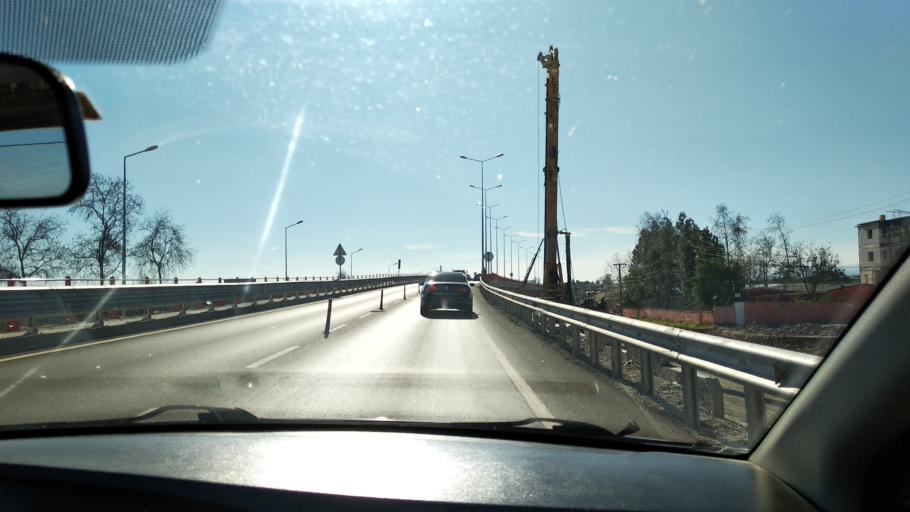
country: TR
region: Mersin
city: Tomuk
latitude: 36.6719
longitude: 34.4080
